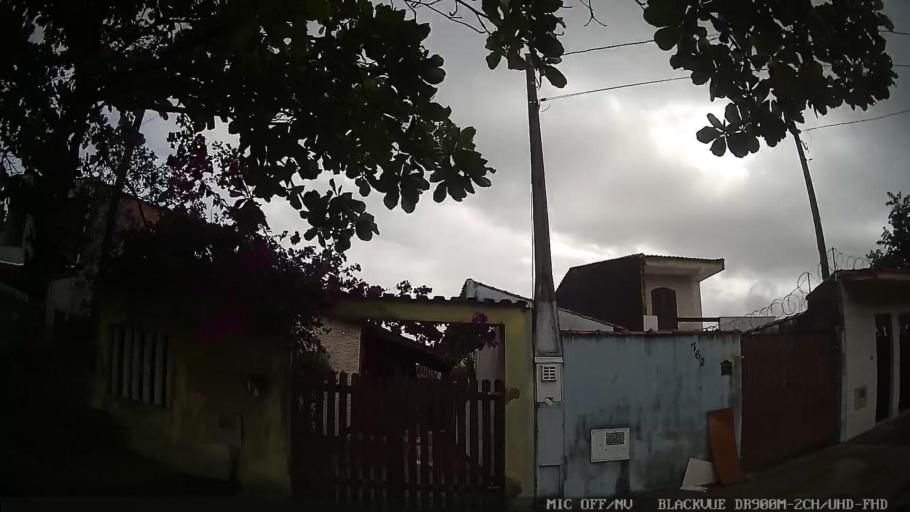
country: BR
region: Sao Paulo
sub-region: Itanhaem
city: Itanhaem
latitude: -24.1911
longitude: -46.8280
